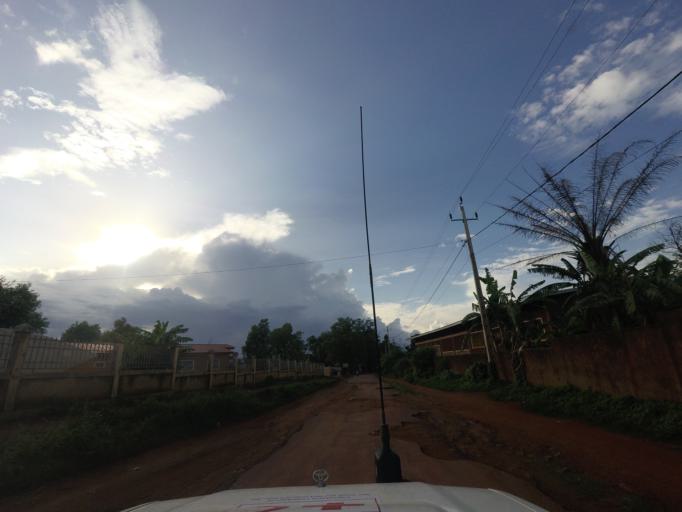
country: GN
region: Nzerekore
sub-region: Nzerekore Prefecture
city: Nzerekore
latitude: 7.7326
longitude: -8.8288
